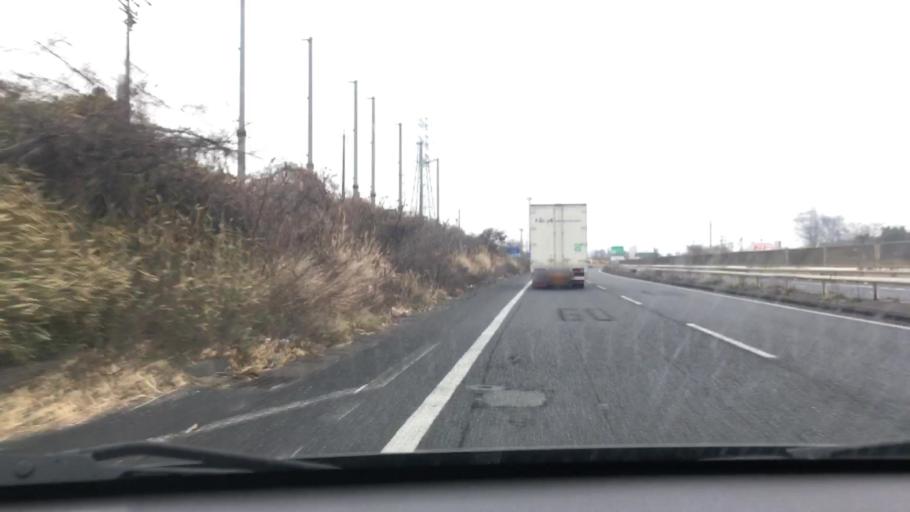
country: JP
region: Mie
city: Ueno-ebisumachi
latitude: 34.7187
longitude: 136.0817
